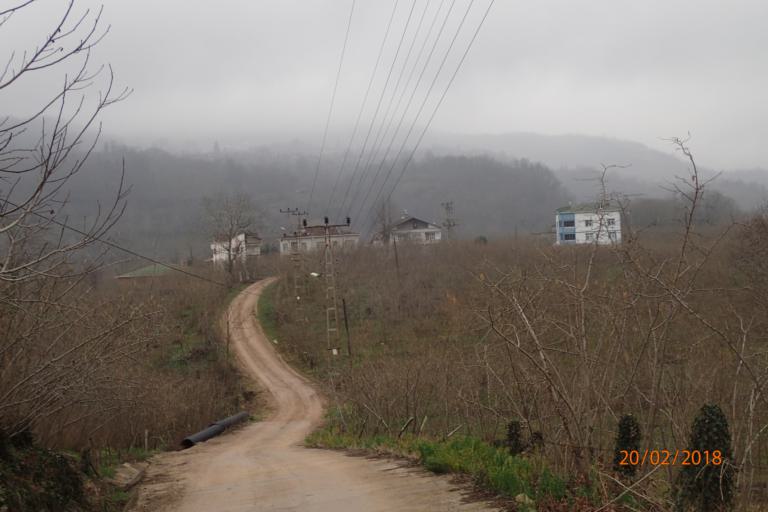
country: TR
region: Ordu
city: Camas
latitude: 40.9476
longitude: 37.5317
